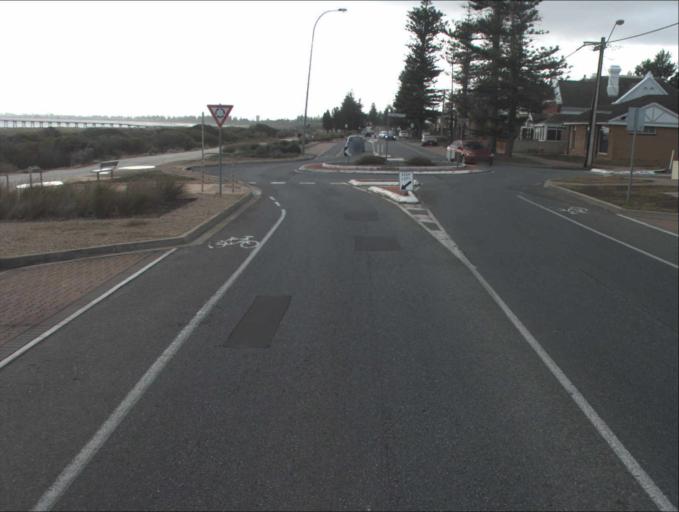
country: AU
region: South Australia
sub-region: Port Adelaide Enfield
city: Birkenhead
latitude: -34.8297
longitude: 138.4838
